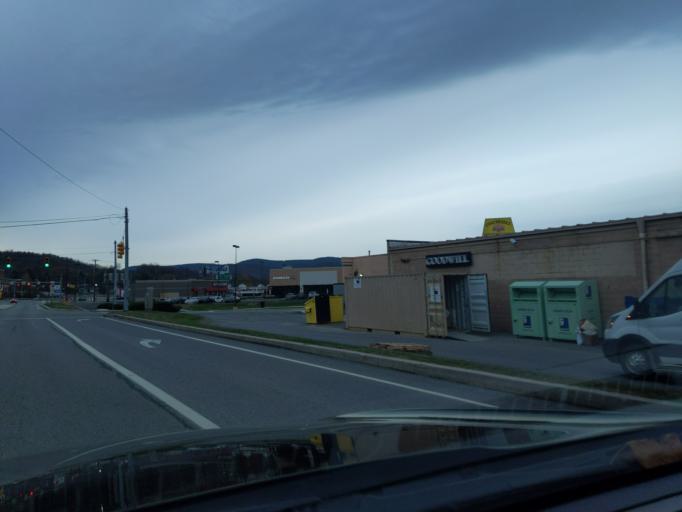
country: US
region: Pennsylvania
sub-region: Blair County
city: Lakemont
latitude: 40.4692
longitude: -78.4047
